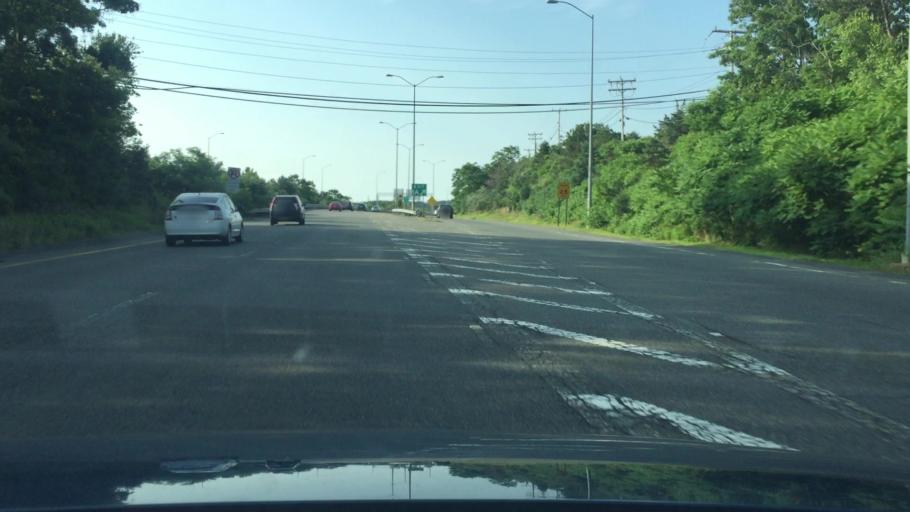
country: US
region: Massachusetts
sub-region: Barnstable County
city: Sagamore
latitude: 41.7859
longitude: -70.5445
